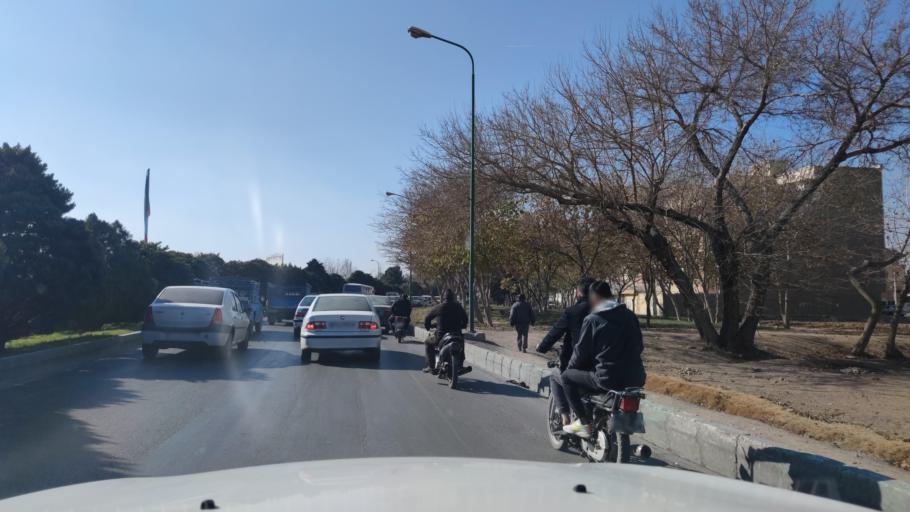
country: IR
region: Isfahan
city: Rehnan
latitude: 32.6824
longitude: 51.6441
